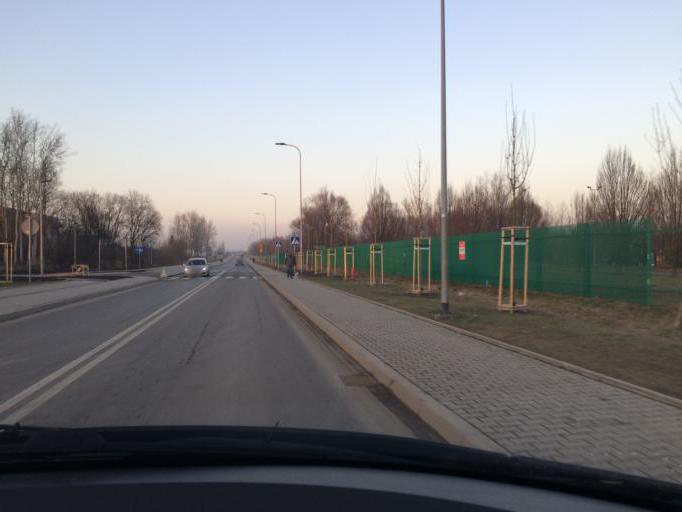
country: PL
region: Lesser Poland Voivodeship
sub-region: Powiat wielicki
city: Czarnochowice
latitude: 50.0243
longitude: 20.0513
